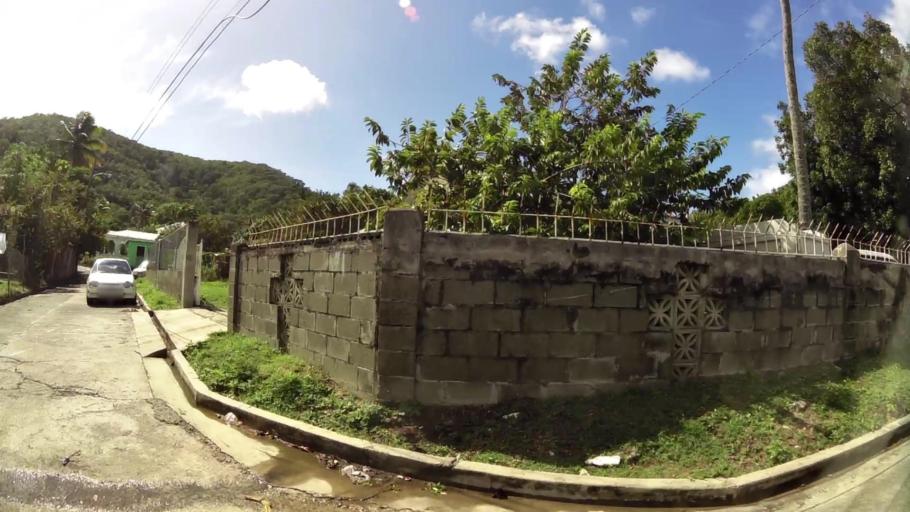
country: AG
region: Saint Mary
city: Bolands
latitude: 17.0647
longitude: -61.8757
